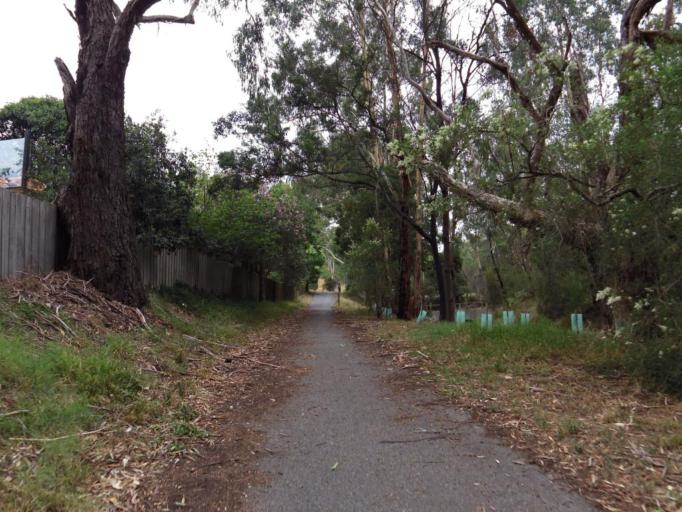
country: AU
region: Victoria
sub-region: Manningham
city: Templestowe Lower
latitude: -37.7606
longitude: 145.1256
